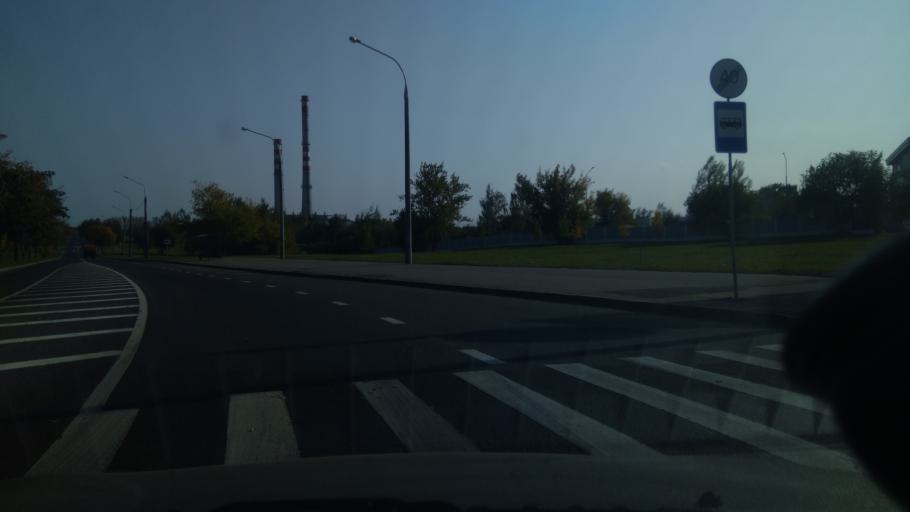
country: BY
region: Minsk
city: Vyaliki Trastsyanets
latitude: 53.8321
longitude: 27.6961
